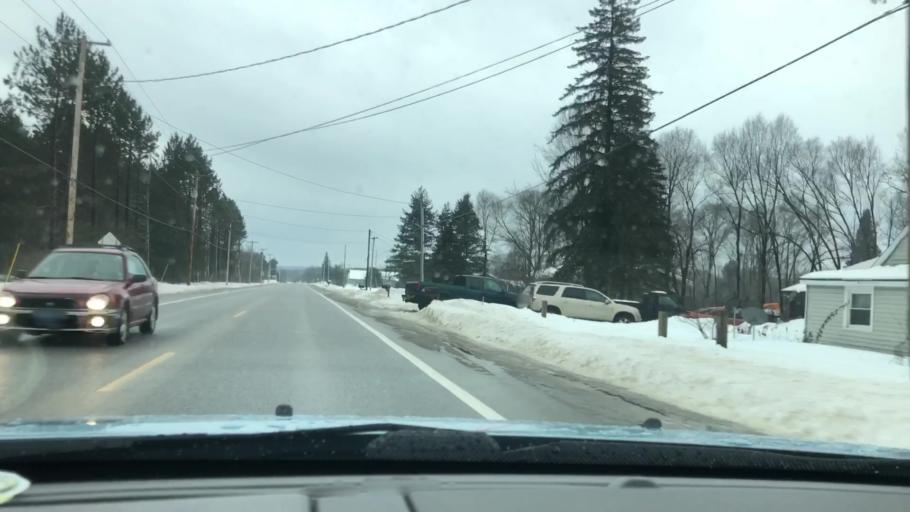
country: US
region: Michigan
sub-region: Charlevoix County
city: East Jordan
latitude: 45.1429
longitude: -85.1192
